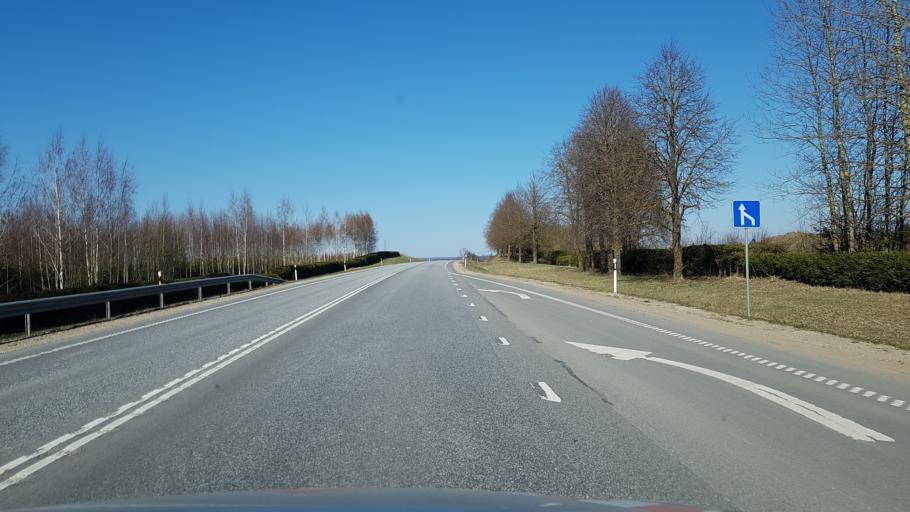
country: EE
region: Tartu
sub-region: Tartu linn
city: Tartu
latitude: 58.4354
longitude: 26.7936
